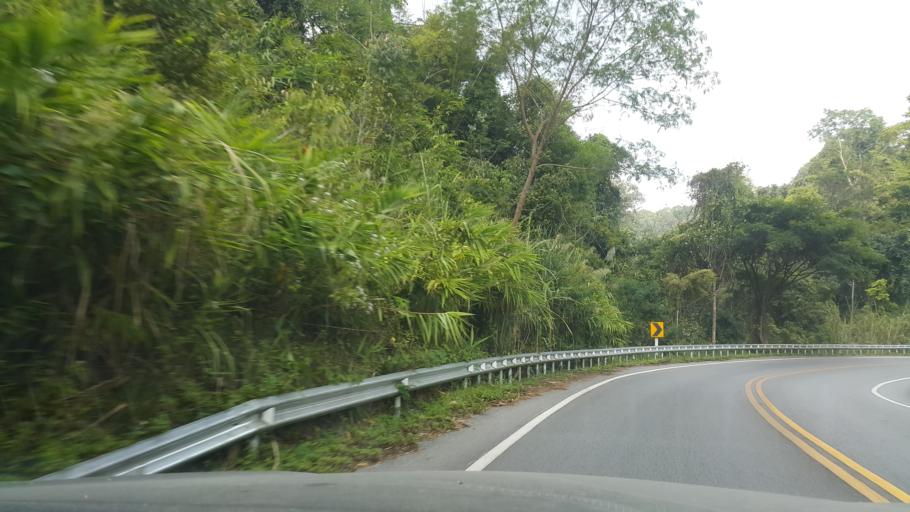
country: TH
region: Lampang
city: Wang Nuea
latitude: 19.0647
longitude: 99.7548
